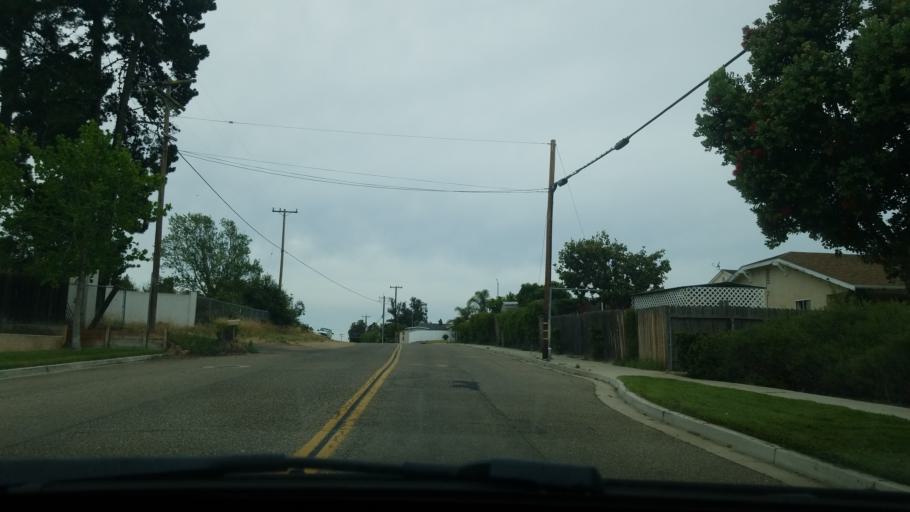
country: US
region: California
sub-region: San Luis Obispo County
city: Nipomo
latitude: 35.0290
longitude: -120.4877
